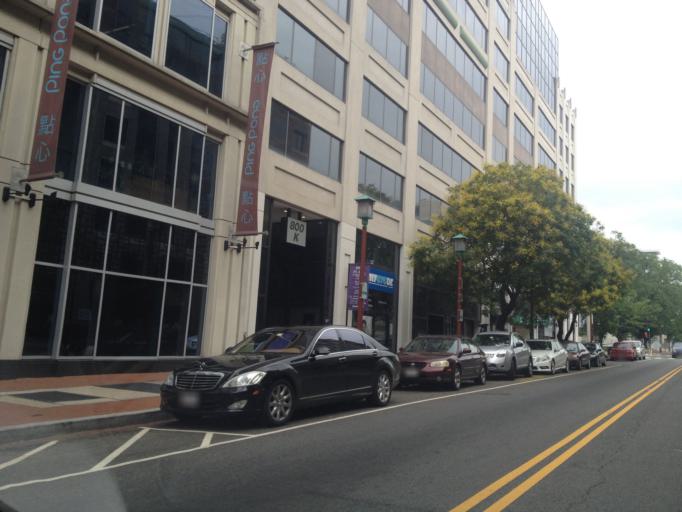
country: US
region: Washington, D.C.
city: Washington, D.C.
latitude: 38.9013
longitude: -77.0220
